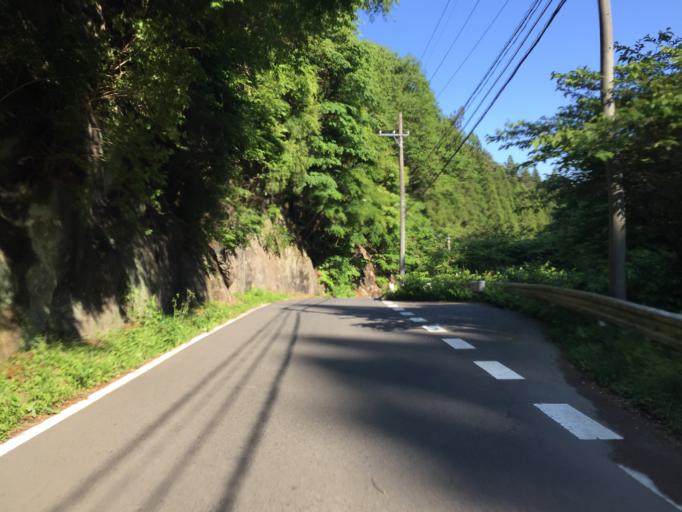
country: JP
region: Ibaraki
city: Kitaibaraki
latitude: 36.8676
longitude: 140.6593
